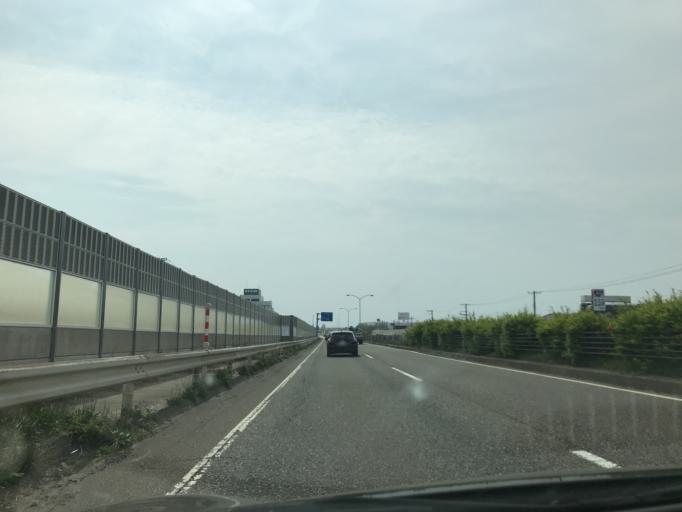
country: JP
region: Niigata
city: Kameda-honcho
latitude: 37.8874
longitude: 139.0774
